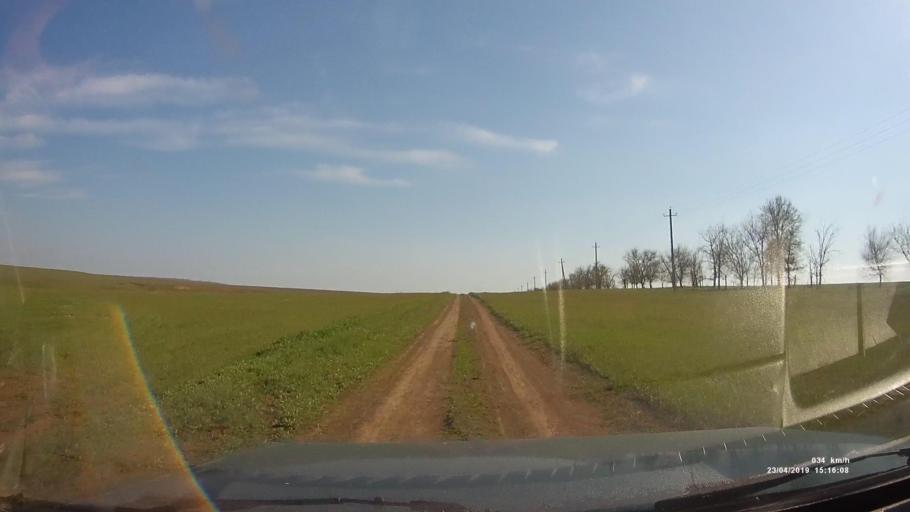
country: RU
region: Rostov
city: Remontnoye
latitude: 46.5355
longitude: 42.9697
